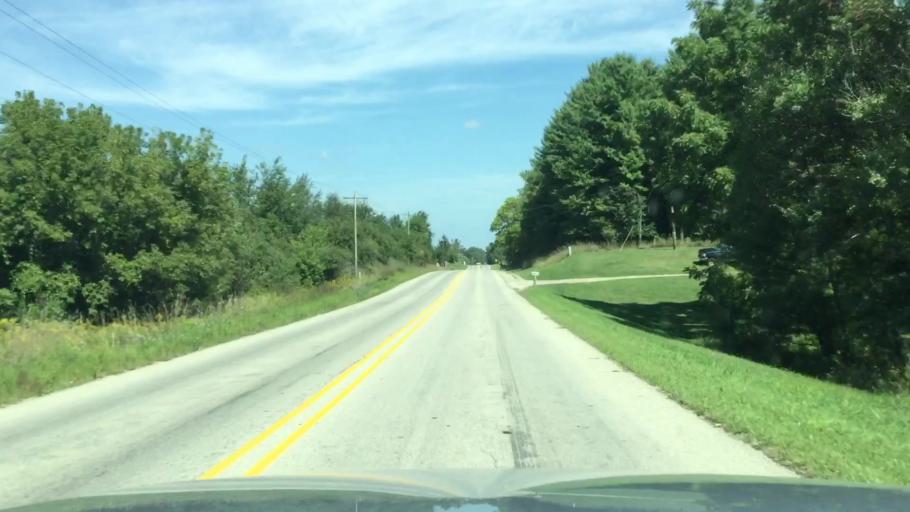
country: US
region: Michigan
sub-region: Lenawee County
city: Manitou Beach-Devils Lake
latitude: 42.0131
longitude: -84.2762
